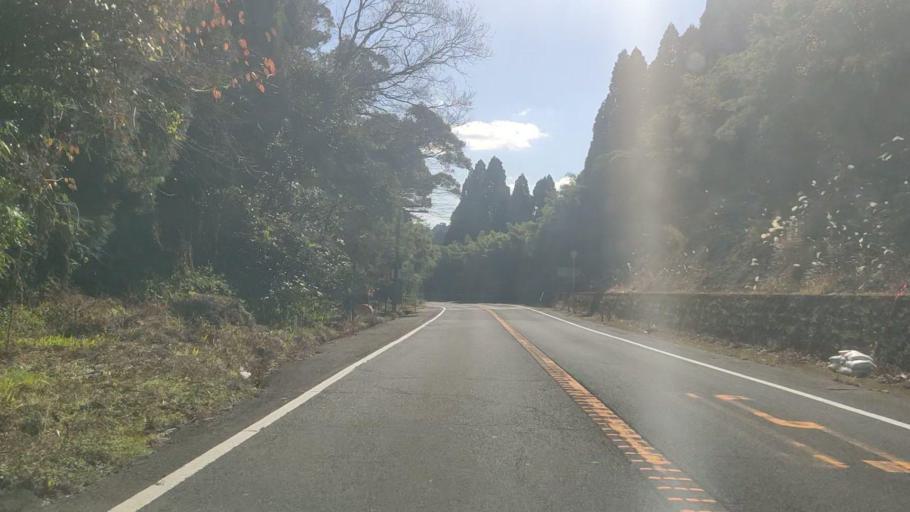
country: JP
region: Kagoshima
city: Kokubu-matsuki
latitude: 31.6644
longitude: 130.8813
